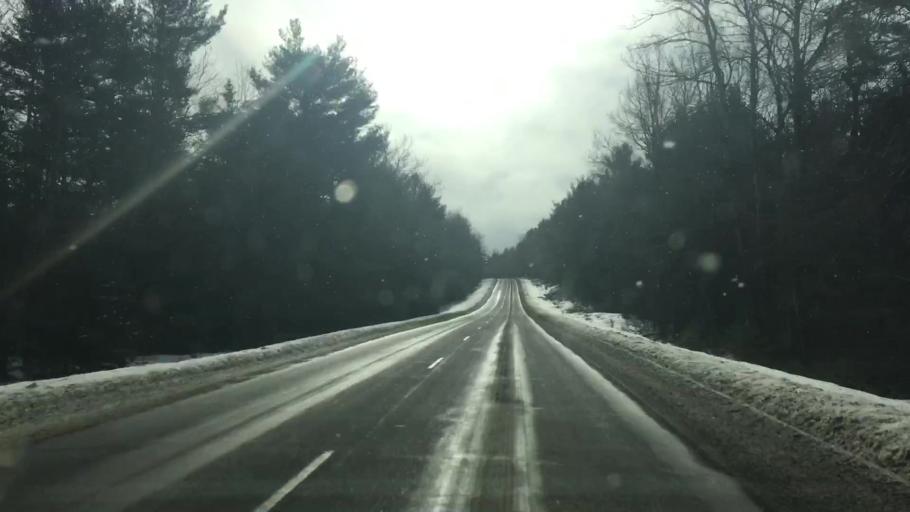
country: US
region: Maine
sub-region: Washington County
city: Calais
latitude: 45.0711
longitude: -67.3315
